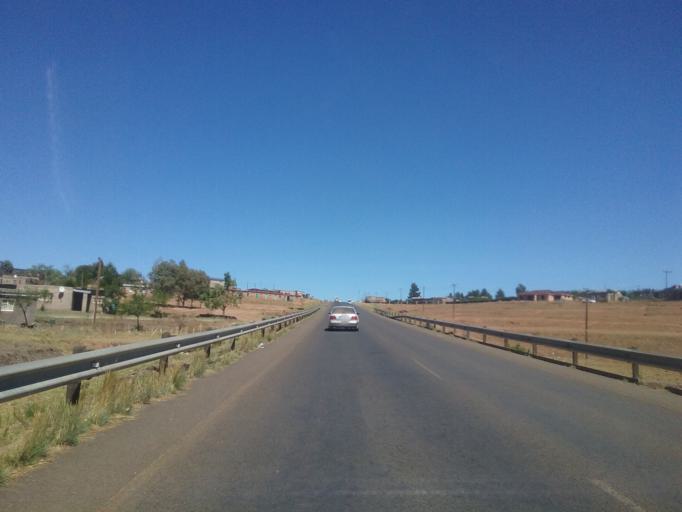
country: LS
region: Quthing
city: Quthing
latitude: -30.3955
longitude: 27.6426
